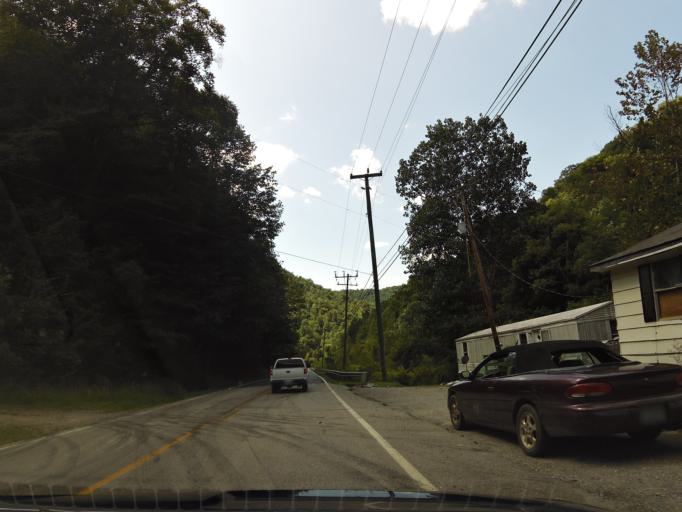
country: US
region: Kentucky
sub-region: Leslie County
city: Hyden
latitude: 37.0208
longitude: -83.3934
